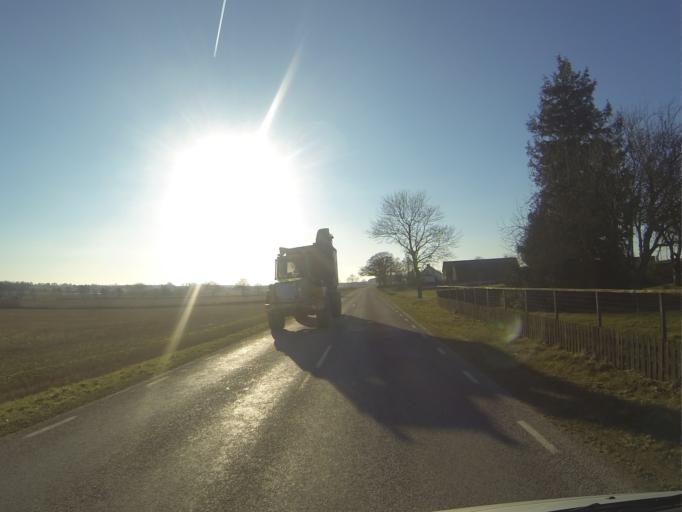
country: SE
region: Skane
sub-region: Hoors Kommun
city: Loberod
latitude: 55.7961
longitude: 13.5562
